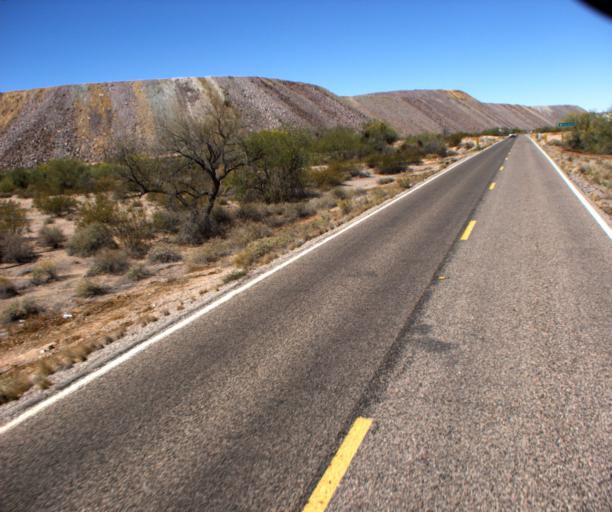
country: US
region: Arizona
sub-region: Pima County
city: Ajo
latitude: 32.3550
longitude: -112.8253
